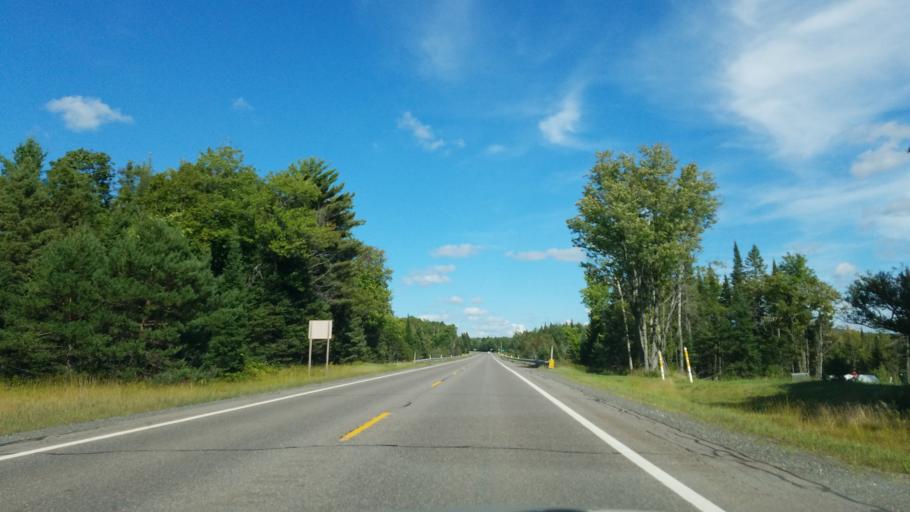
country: US
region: Michigan
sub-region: Baraga County
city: L'Anse
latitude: 46.5480
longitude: -88.5316
